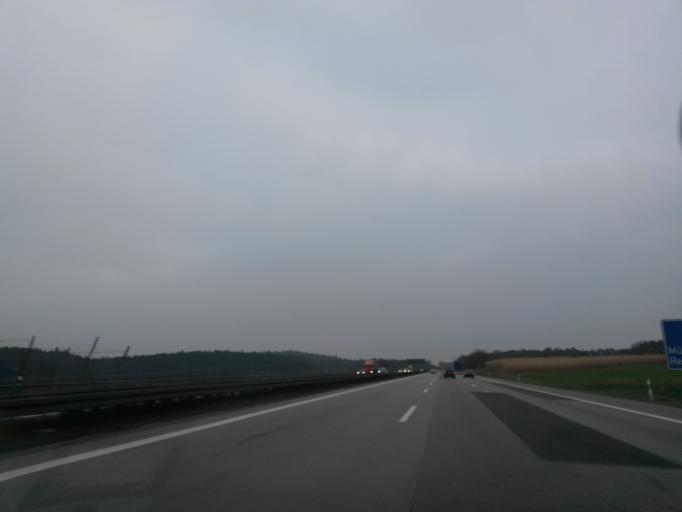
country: DE
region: Bavaria
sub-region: Upper Bavaria
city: Rohrbach
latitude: 48.6405
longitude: 11.5193
